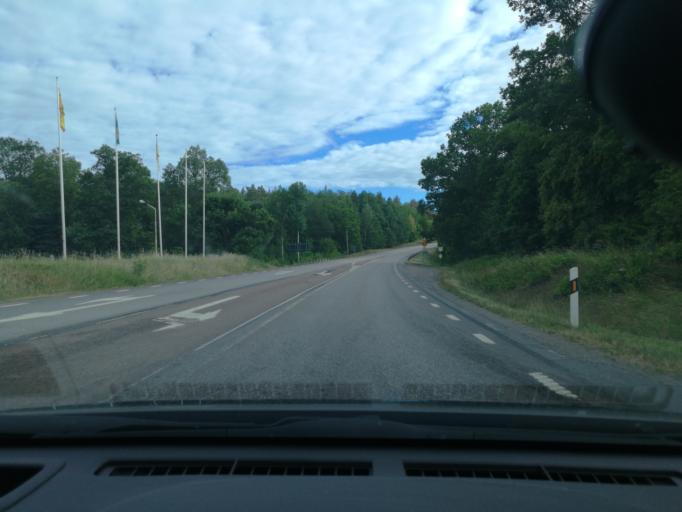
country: SE
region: Kalmar
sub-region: Vasterviks Kommun
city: Ankarsrum
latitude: 57.5712
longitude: 16.4843
